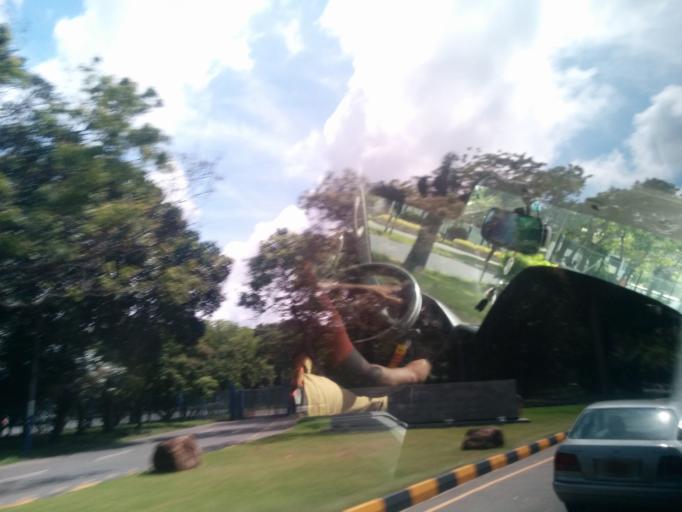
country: LK
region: Western
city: Katunayaka
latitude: 7.1702
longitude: 79.8845
